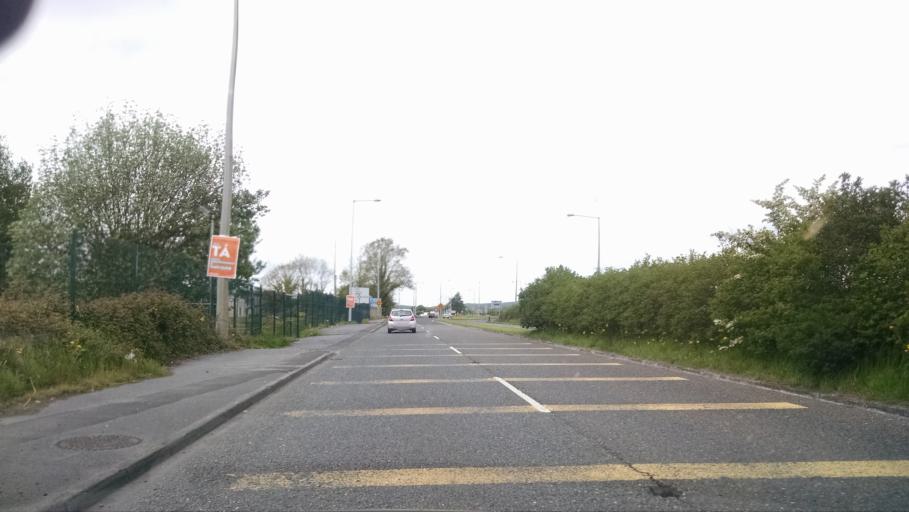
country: IE
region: Munster
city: Moyross
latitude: 52.6753
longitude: -8.6788
